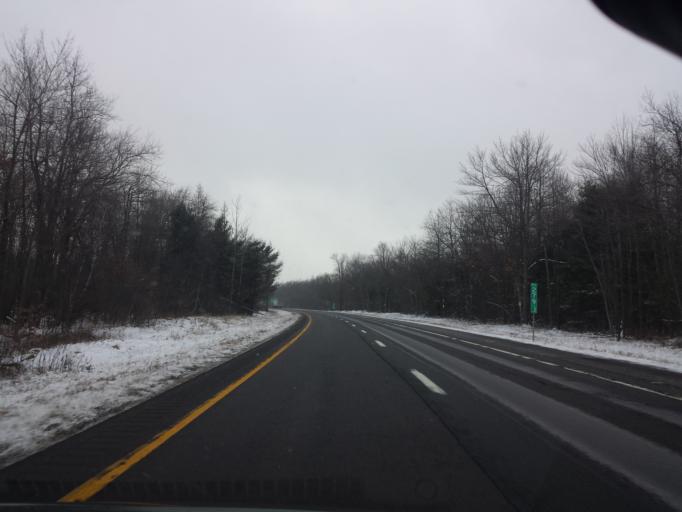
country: US
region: Pennsylvania
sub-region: Carbon County
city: Towamensing Trails
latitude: 41.0806
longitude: -75.6605
